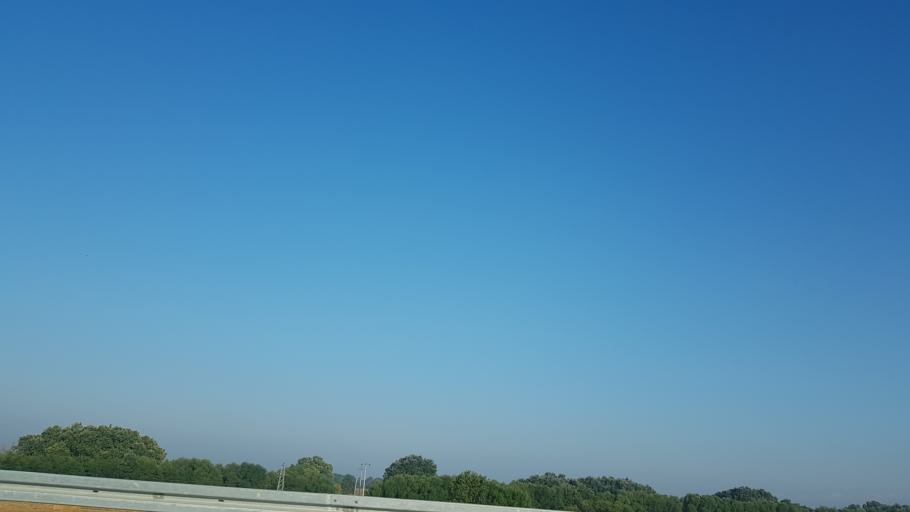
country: TR
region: Bursa
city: Karacabey
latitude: 40.1558
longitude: 28.3121
